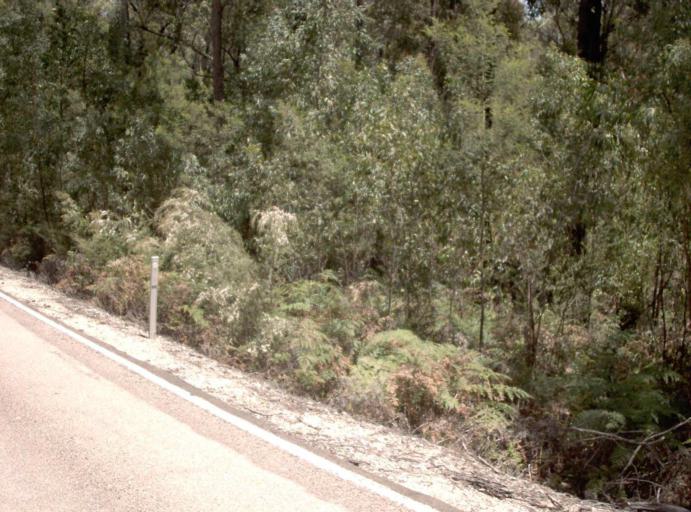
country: AU
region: Victoria
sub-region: East Gippsland
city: Lakes Entrance
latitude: -37.6493
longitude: 147.8926
